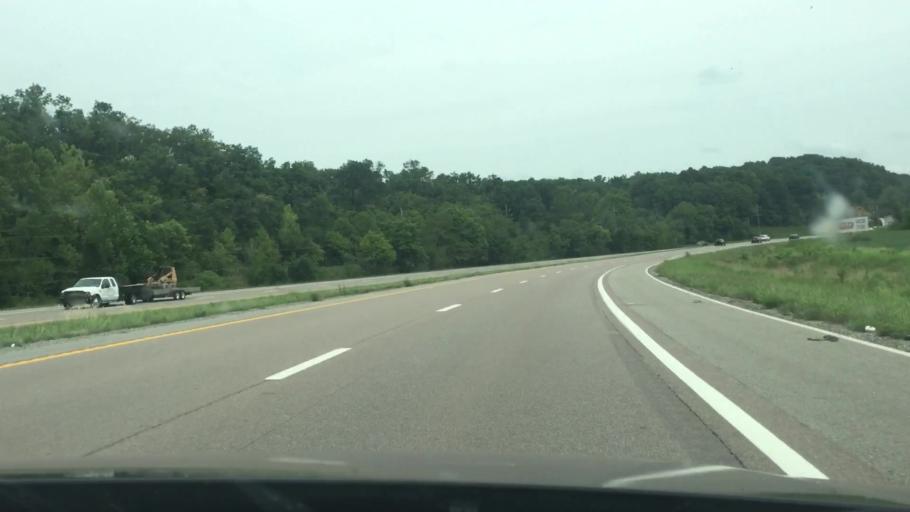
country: US
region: Missouri
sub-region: Miller County
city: Lake Ozark
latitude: 38.2401
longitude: -92.6176
